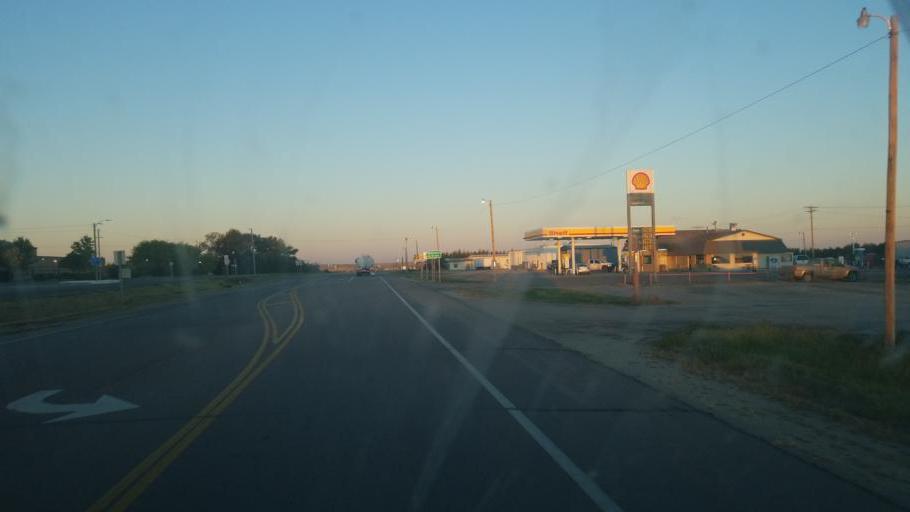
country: US
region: Kansas
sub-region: Wallace County
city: Sharon Springs
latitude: 38.9024
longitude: -101.7508
